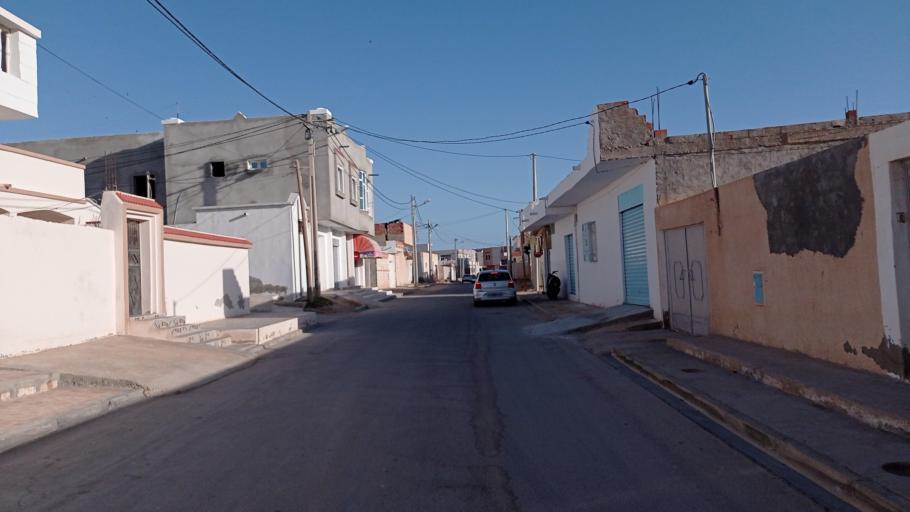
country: TN
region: Qabis
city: Gabes
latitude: 33.8541
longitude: 10.1206
